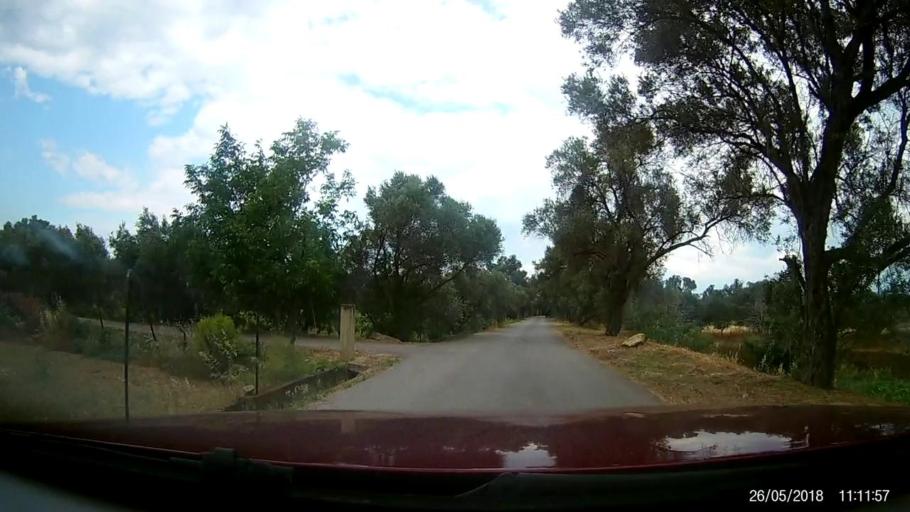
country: GR
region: Central Greece
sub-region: Nomos Evvoias
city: Mytikas
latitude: 38.4482
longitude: 23.6584
